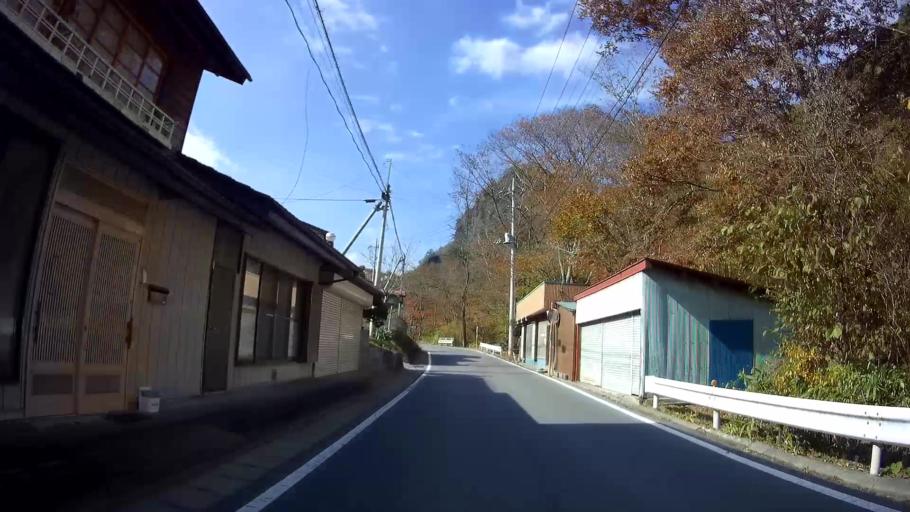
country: JP
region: Gunma
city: Nakanojomachi
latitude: 36.5137
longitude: 138.7724
